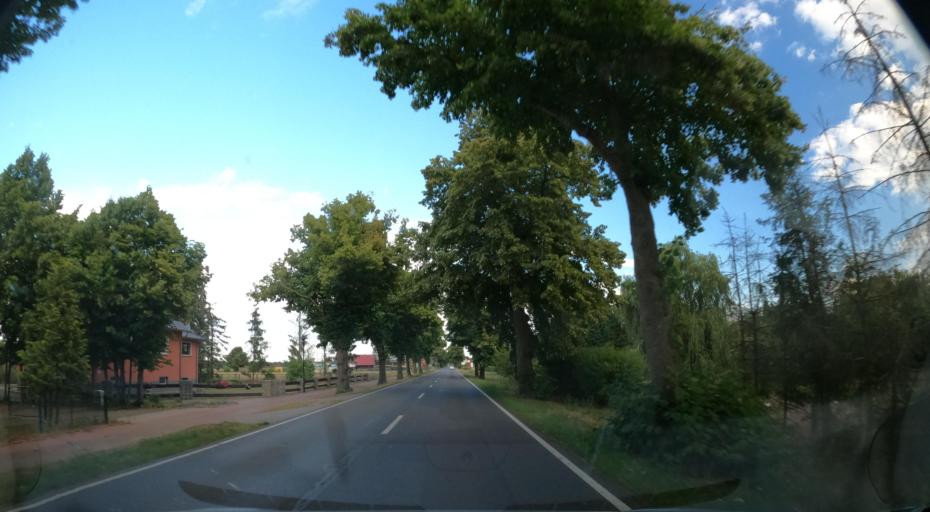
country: DE
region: Brandenburg
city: Brussow
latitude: 53.4583
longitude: 14.1901
